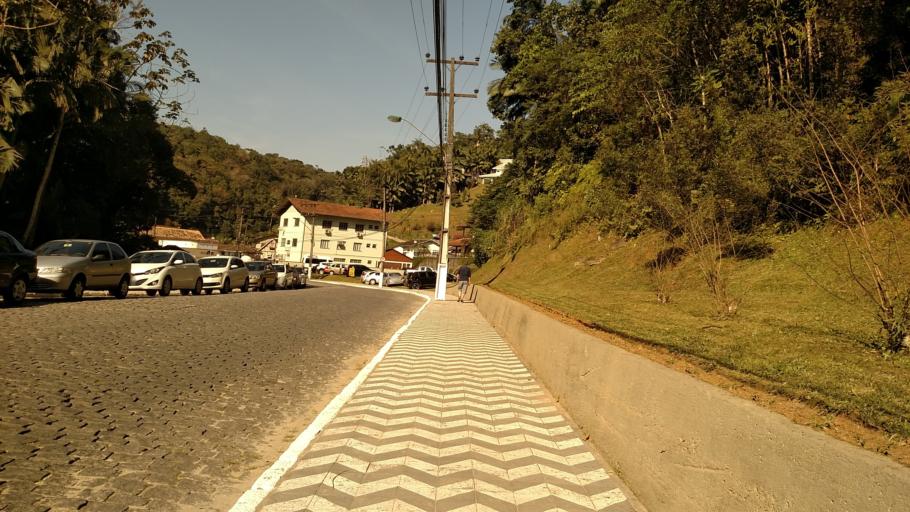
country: BR
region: Santa Catarina
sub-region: Pomerode
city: Pomerode
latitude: -26.7303
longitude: -49.0689
